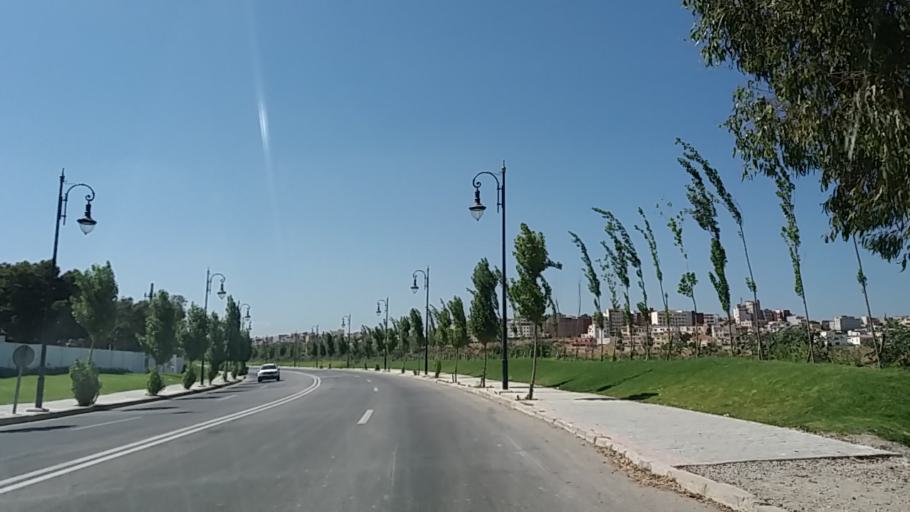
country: MA
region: Tanger-Tetouan
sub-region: Tanger-Assilah
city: Tangier
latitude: 35.7771
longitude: -5.7625
